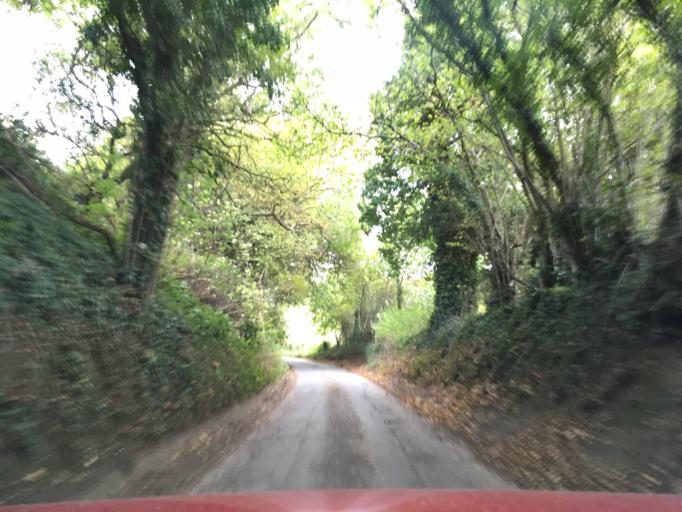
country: GB
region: England
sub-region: South Gloucestershire
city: Horton
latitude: 51.5881
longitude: -2.3379
